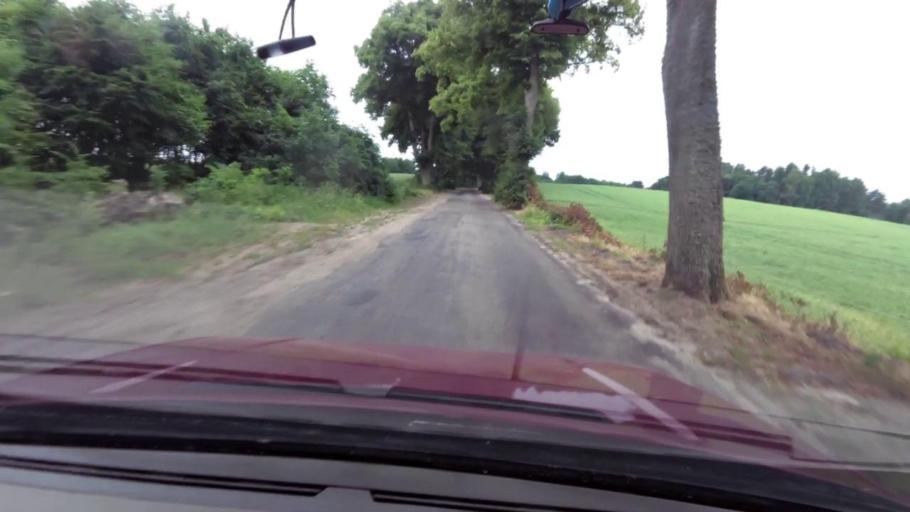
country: PL
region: Pomeranian Voivodeship
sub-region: Powiat slupski
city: Kepice
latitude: 54.1899
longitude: 16.7961
